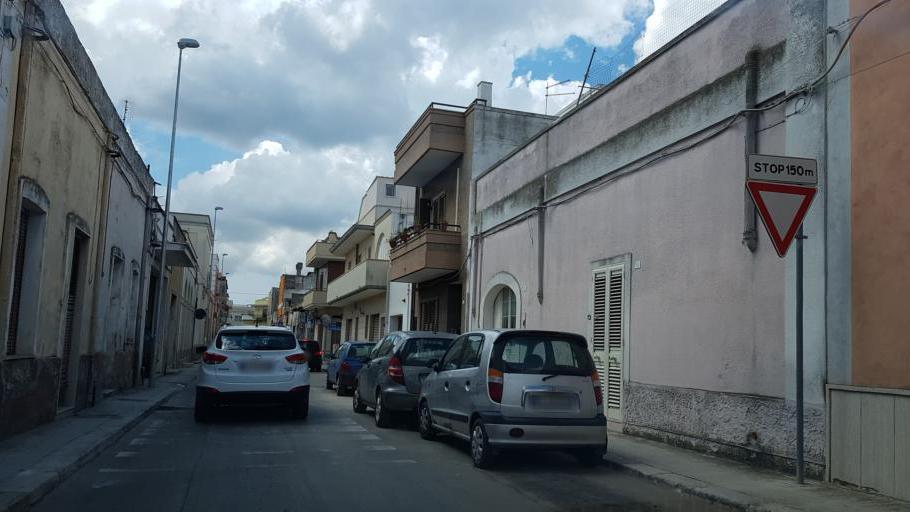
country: IT
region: Apulia
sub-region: Provincia di Brindisi
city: San Pancrazio Salentino
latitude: 40.4195
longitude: 17.8406
